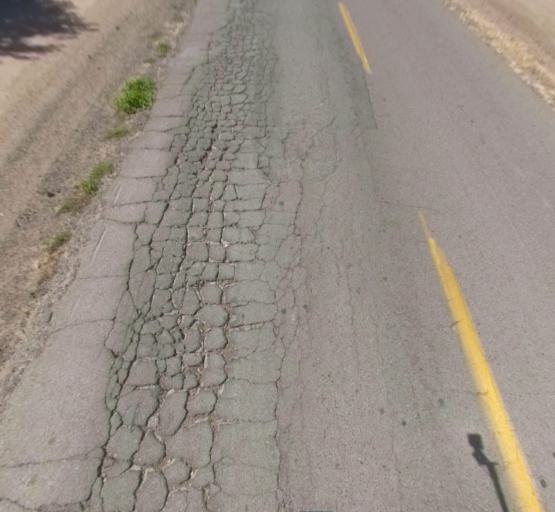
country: US
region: California
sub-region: Madera County
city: Chowchilla
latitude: 37.0245
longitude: -120.3833
